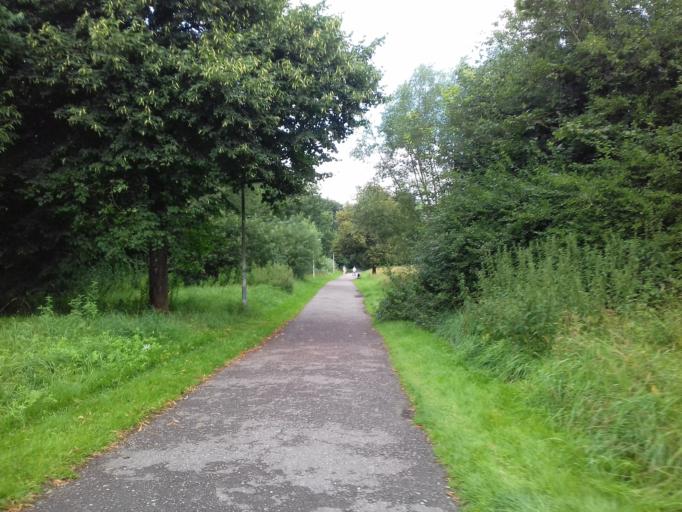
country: DE
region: Schleswig-Holstein
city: Kronshagen
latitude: 54.3203
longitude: 10.0606
